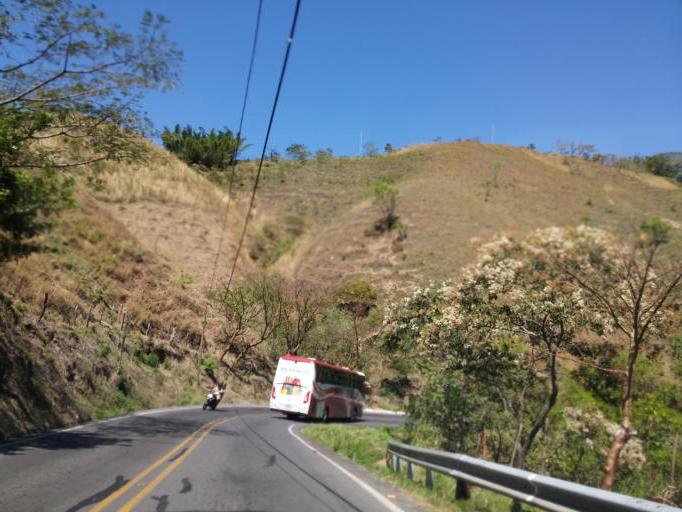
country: CR
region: Heredia
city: Colon
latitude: 9.8869
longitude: -84.2250
